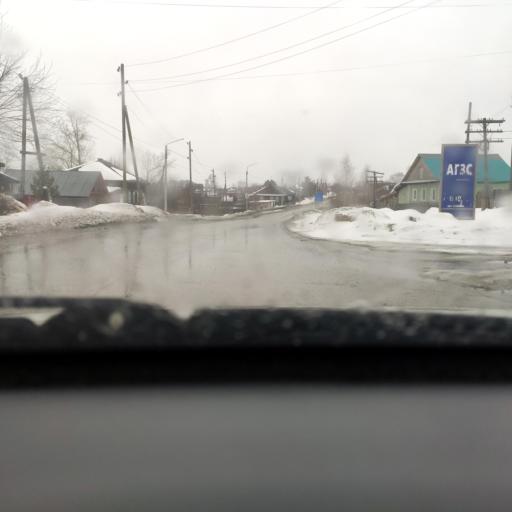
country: RU
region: Perm
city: Yugo-Kamskiy
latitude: 57.7036
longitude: 55.6071
